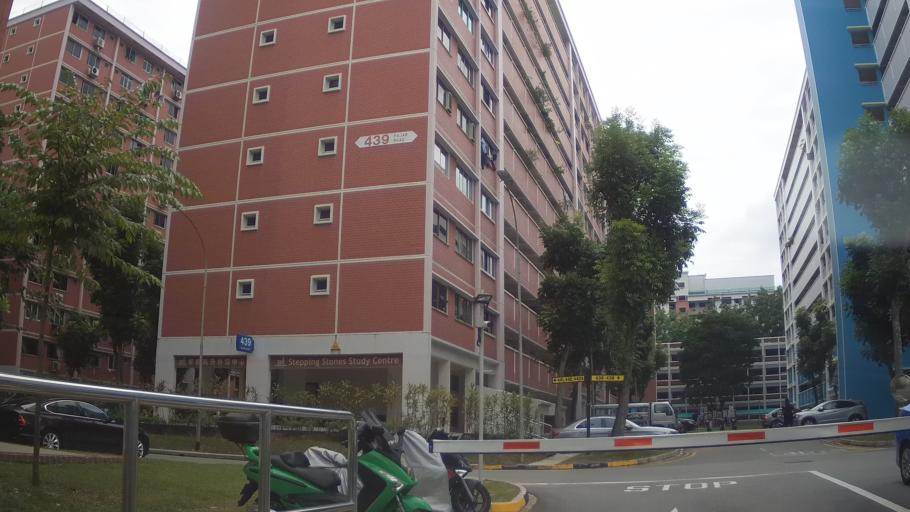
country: MY
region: Johor
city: Johor Bahru
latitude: 1.3833
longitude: 103.7698
